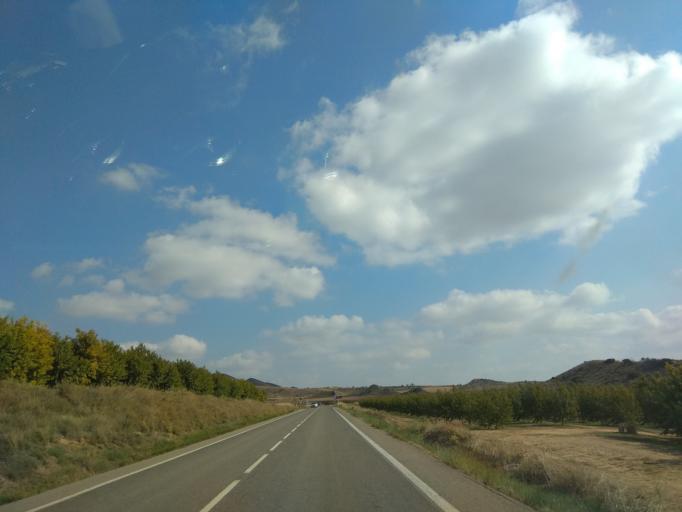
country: ES
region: Catalonia
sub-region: Provincia de Lleida
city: Alfarras
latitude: 41.8247
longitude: 0.5860
